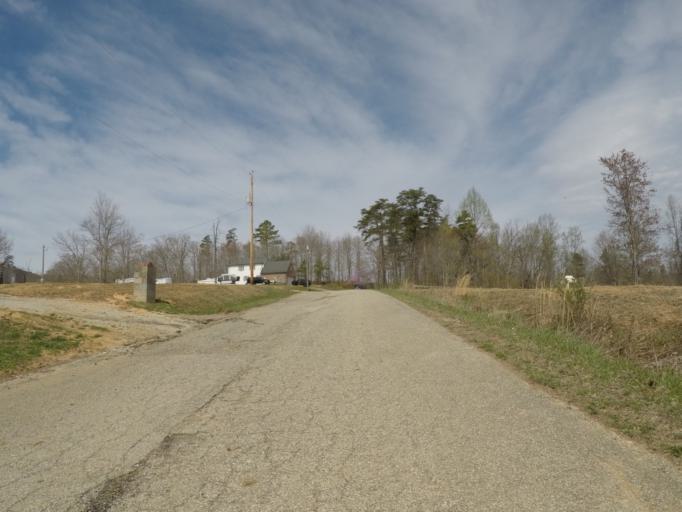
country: US
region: West Virginia
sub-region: Cabell County
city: Pea Ridge
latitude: 38.3251
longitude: -82.3512
